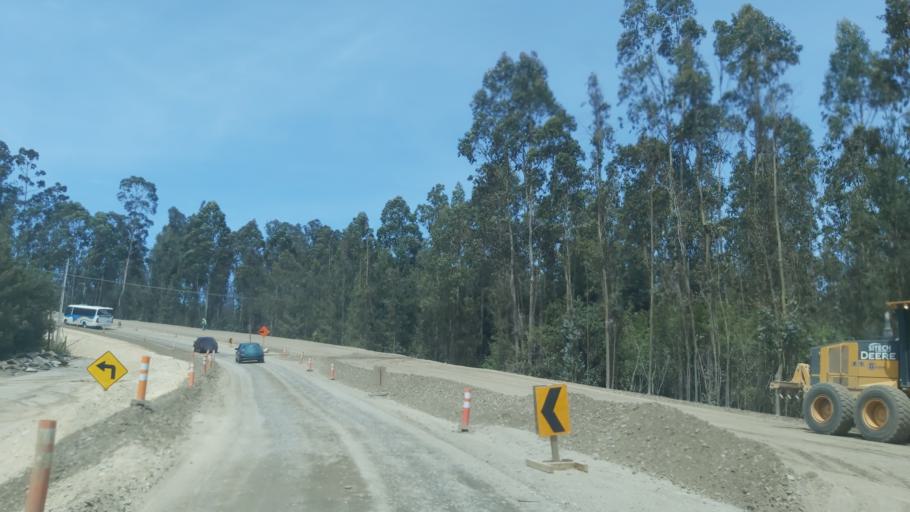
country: CL
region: Maule
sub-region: Provincia de Talca
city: Constitucion
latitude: -35.3869
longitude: -72.4213
